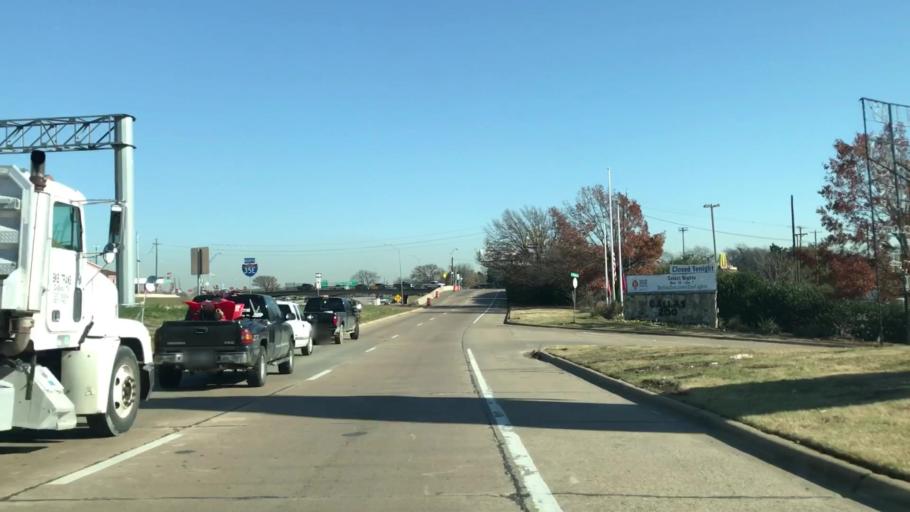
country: US
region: Texas
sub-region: Dallas County
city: Dallas
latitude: 32.7439
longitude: -96.8146
